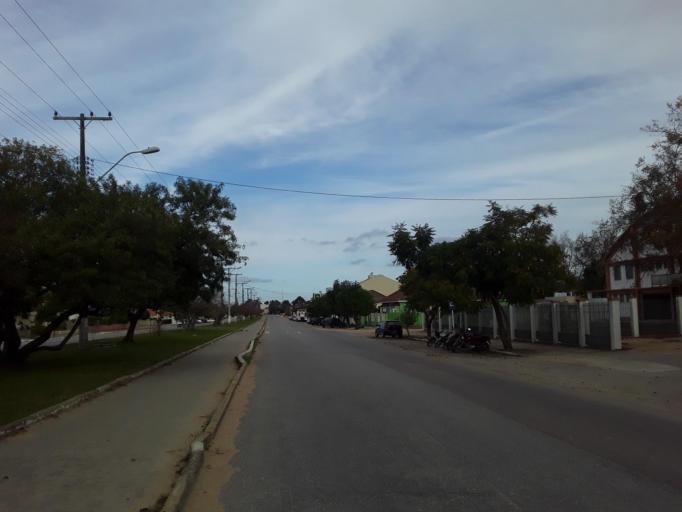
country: BR
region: Rio Grande do Sul
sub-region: Sao Lourenco Do Sul
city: Sao Lourenco do Sul
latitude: -31.3533
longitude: -51.9891
